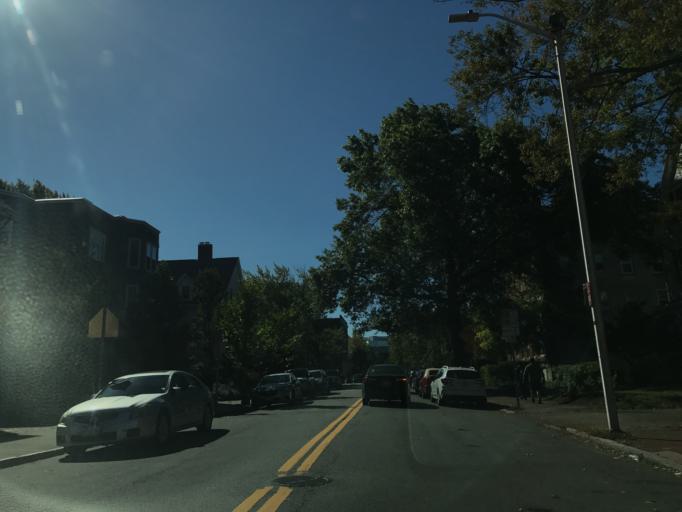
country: US
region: Massachusetts
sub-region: Middlesex County
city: Cambridge
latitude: 42.3823
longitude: -71.1162
